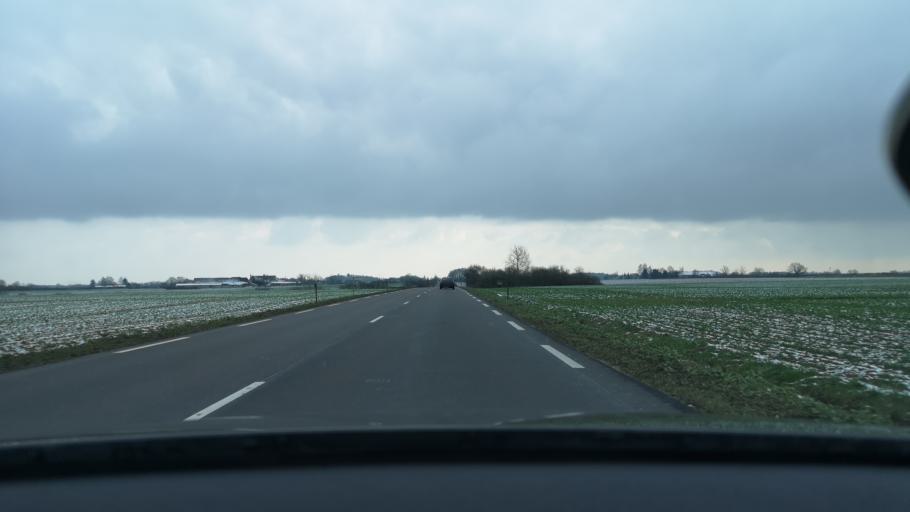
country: FR
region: Bourgogne
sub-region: Departement de Saone-et-Loire
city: Saint-Martin-en-Bresse
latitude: 46.7458
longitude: 5.0588
